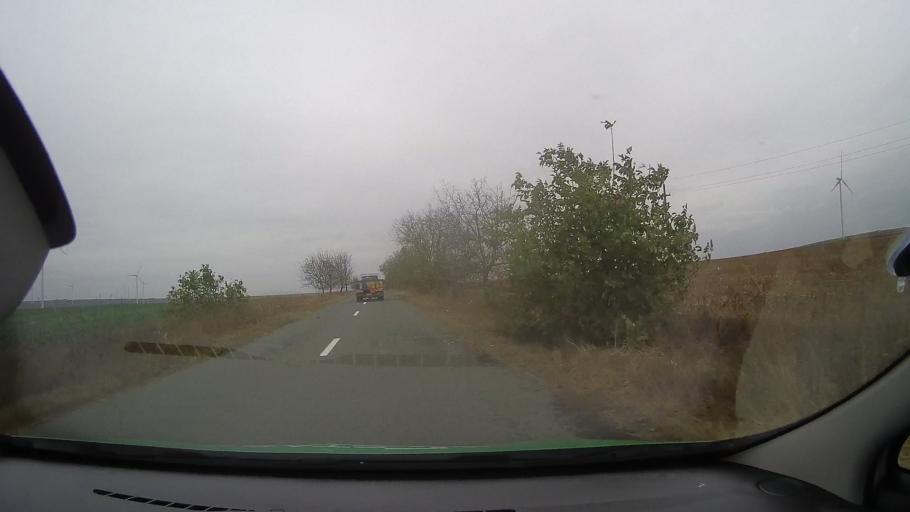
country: RO
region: Constanta
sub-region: Comuna Targusor
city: Targusor
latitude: 44.4801
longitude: 28.3741
